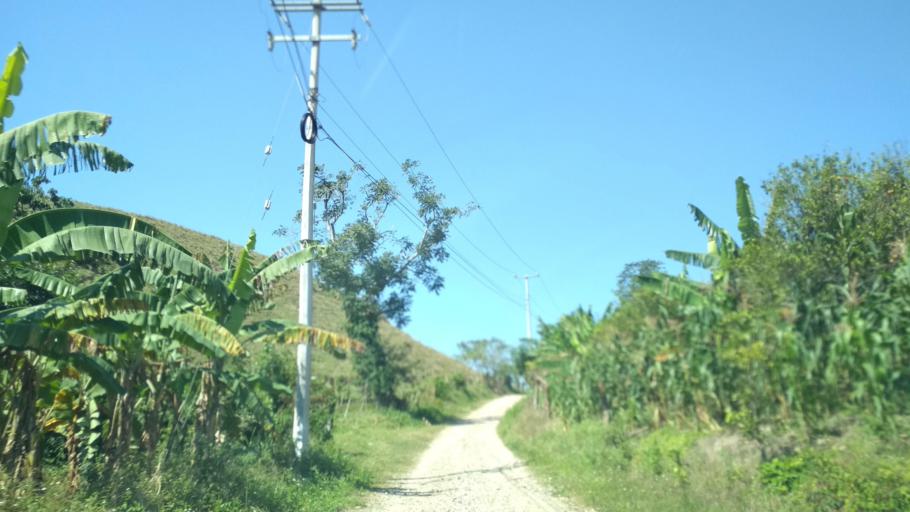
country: MX
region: Veracruz
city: Gutierrez Zamora
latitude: 20.4892
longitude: -97.1642
